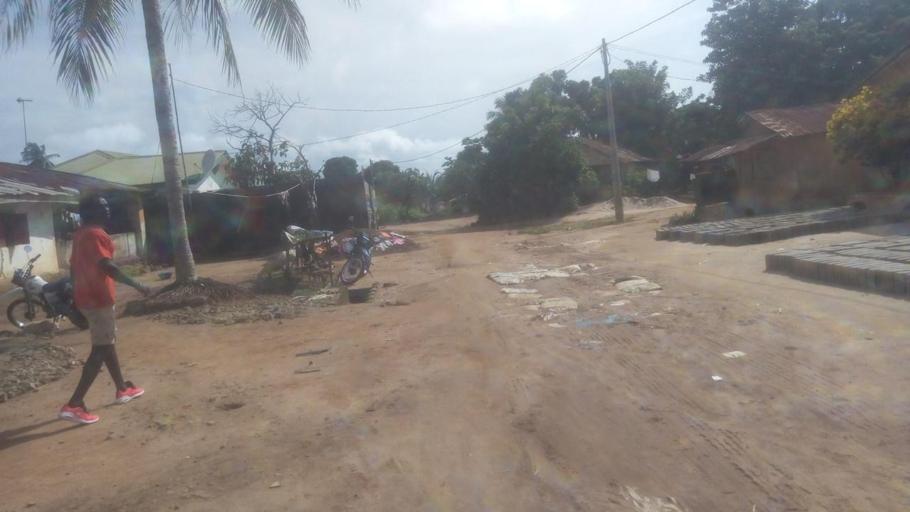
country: SL
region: Northern Province
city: Masoyila
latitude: 8.6118
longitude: -13.1908
